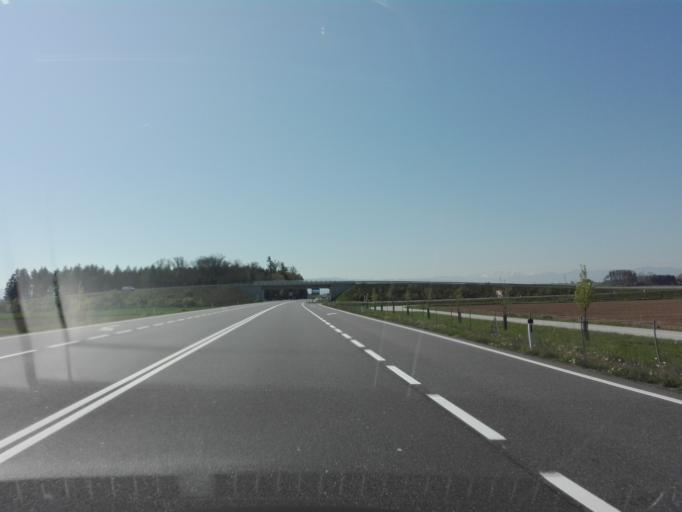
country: AT
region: Lower Austria
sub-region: Politischer Bezirk Amstetten
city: Haidershofen
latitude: 48.1217
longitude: 14.4488
